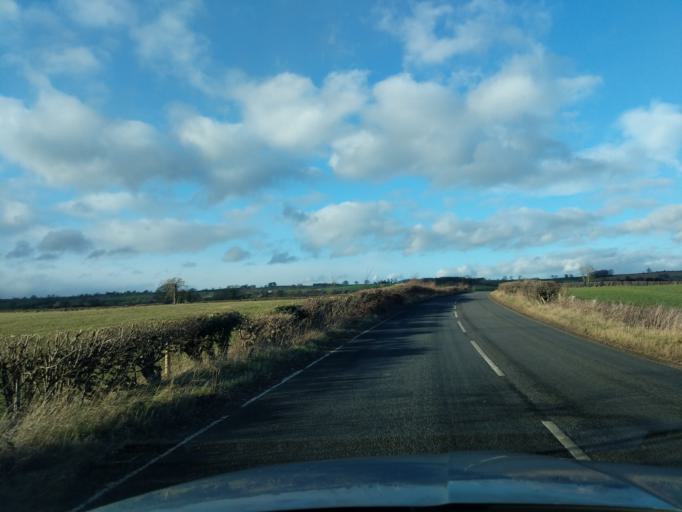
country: GB
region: England
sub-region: North Yorkshire
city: Catterick Garrison
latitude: 54.3276
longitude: -1.6848
